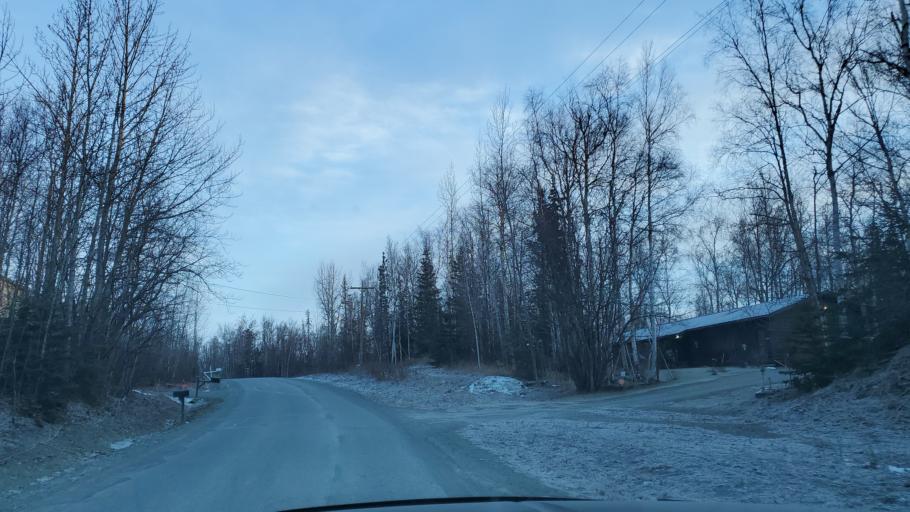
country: US
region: Alaska
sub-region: Matanuska-Susitna Borough
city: Lakes
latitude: 61.6050
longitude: -149.3171
